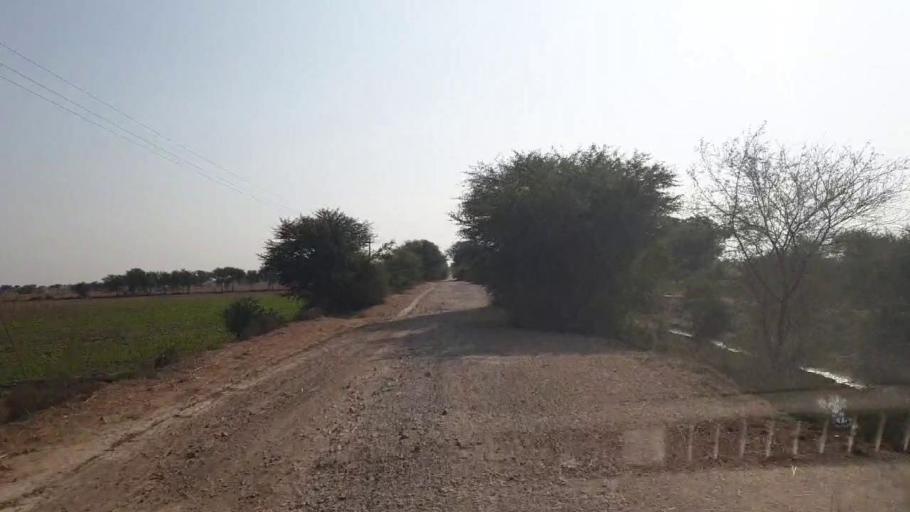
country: PK
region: Sindh
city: Kario
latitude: 24.9113
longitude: 68.6497
